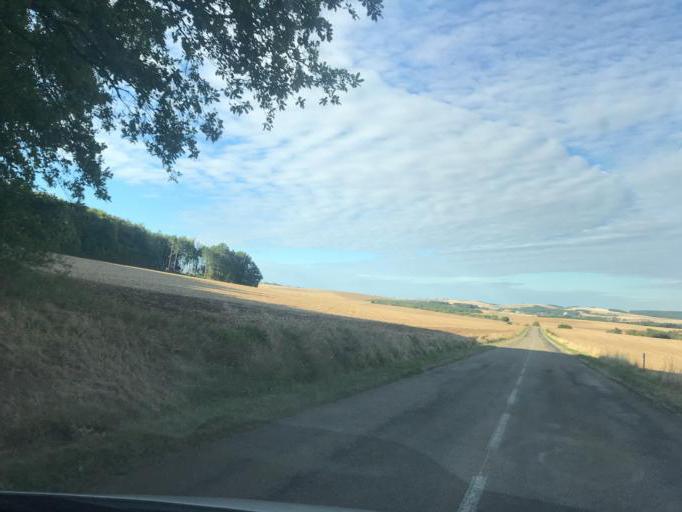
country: FR
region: Bourgogne
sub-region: Departement de l'Yonne
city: Fontenailles
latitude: 47.5808
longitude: 3.4634
